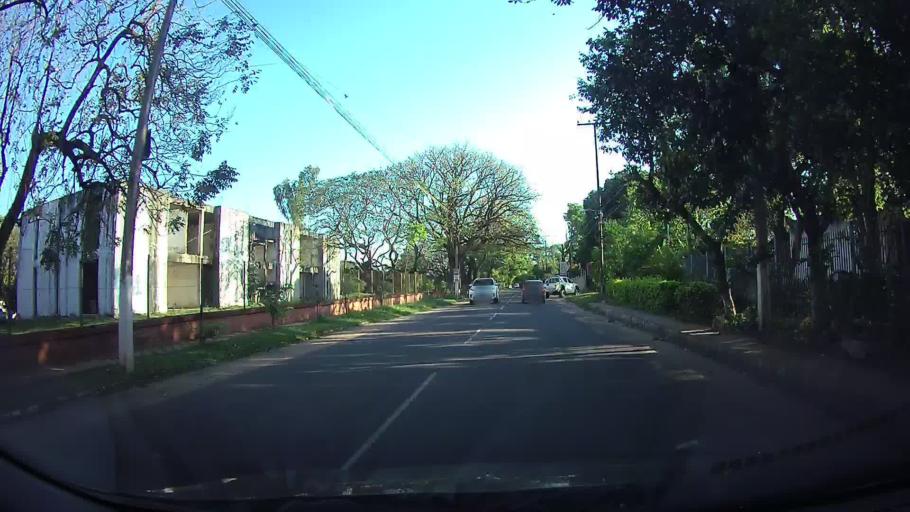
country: PY
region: Central
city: Fernando de la Mora
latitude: -25.3413
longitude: -57.5315
